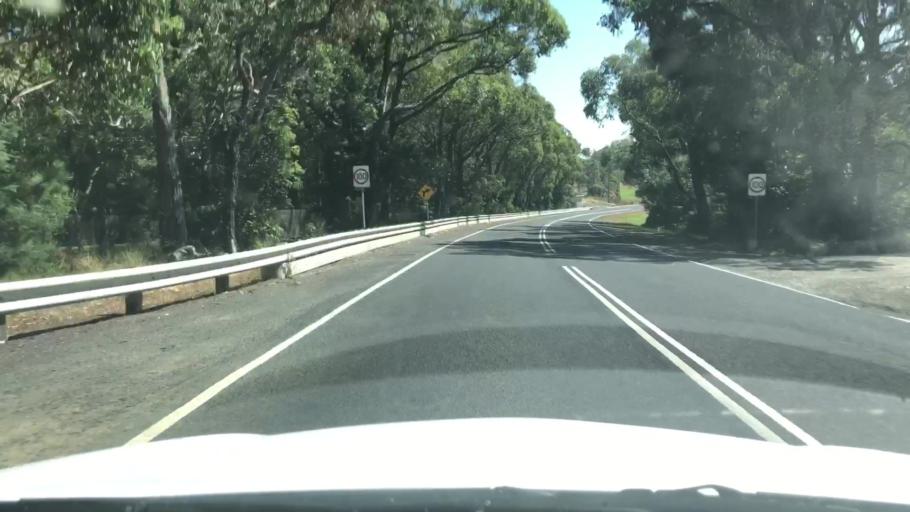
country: AU
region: Victoria
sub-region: Yarra Ranges
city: Selby
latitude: -37.9383
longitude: 145.4033
